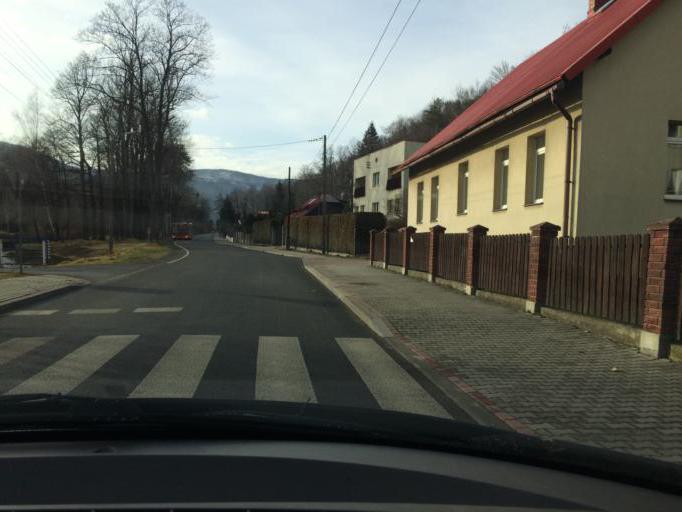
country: PL
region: Silesian Voivodeship
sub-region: Powiat bielski
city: Bystra
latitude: 49.7628
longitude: 19.0666
